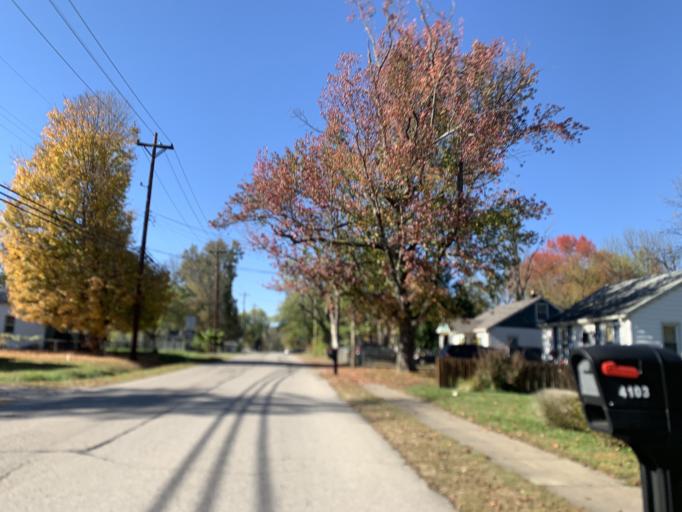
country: US
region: Kentucky
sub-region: Jefferson County
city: Saint Dennis
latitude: 38.1912
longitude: -85.8711
